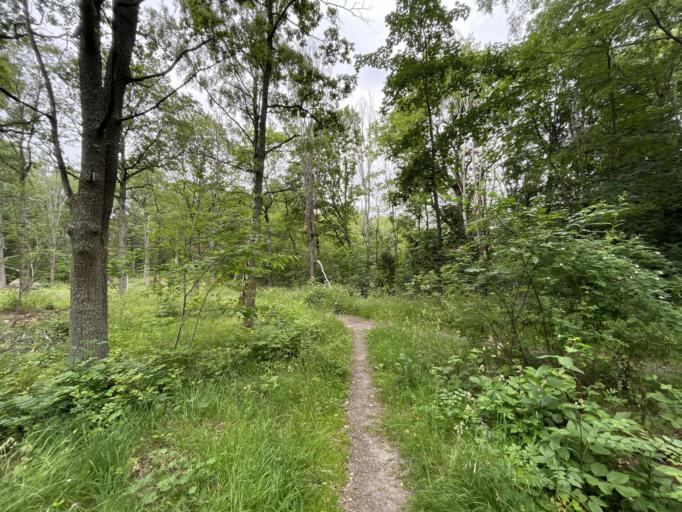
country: SE
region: Stockholm
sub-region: Lidingo
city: Lidingoe
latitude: 59.3348
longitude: 18.1401
